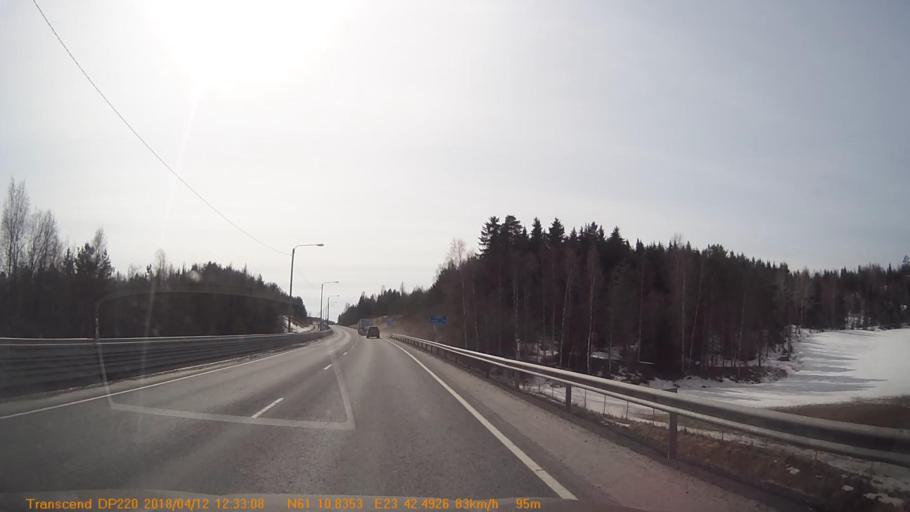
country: FI
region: Pirkanmaa
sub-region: Etelae-Pirkanmaa
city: Kylmaekoski
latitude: 61.1803
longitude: 23.7080
